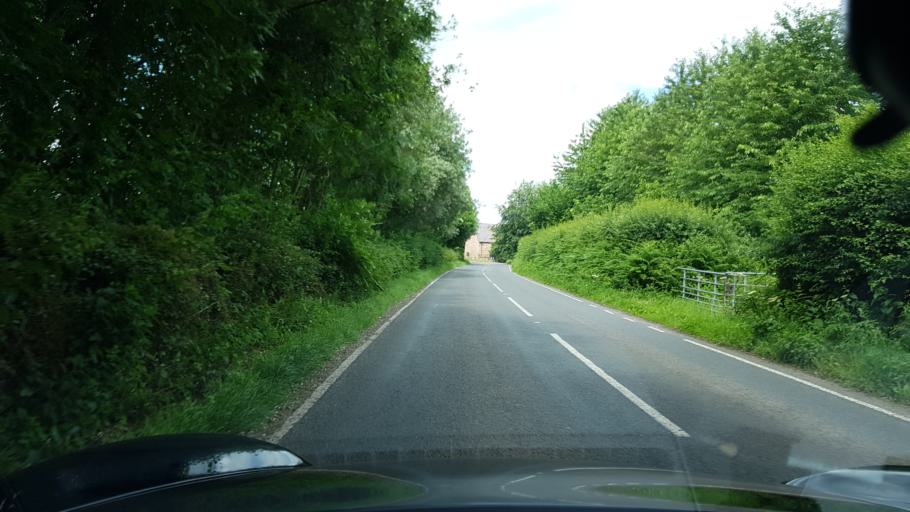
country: GB
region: Wales
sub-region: Monmouthshire
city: Llanarth
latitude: 51.7492
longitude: -2.9456
